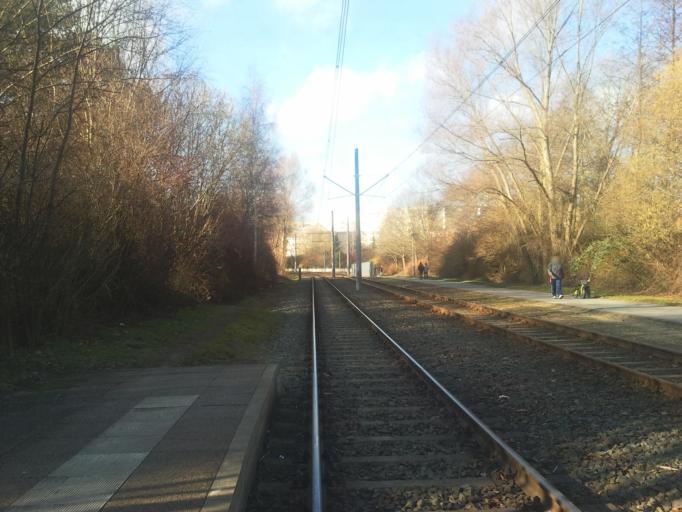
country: DE
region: Mecklenburg-Vorpommern
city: Dierkow-West
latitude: 54.1120
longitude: 12.1504
